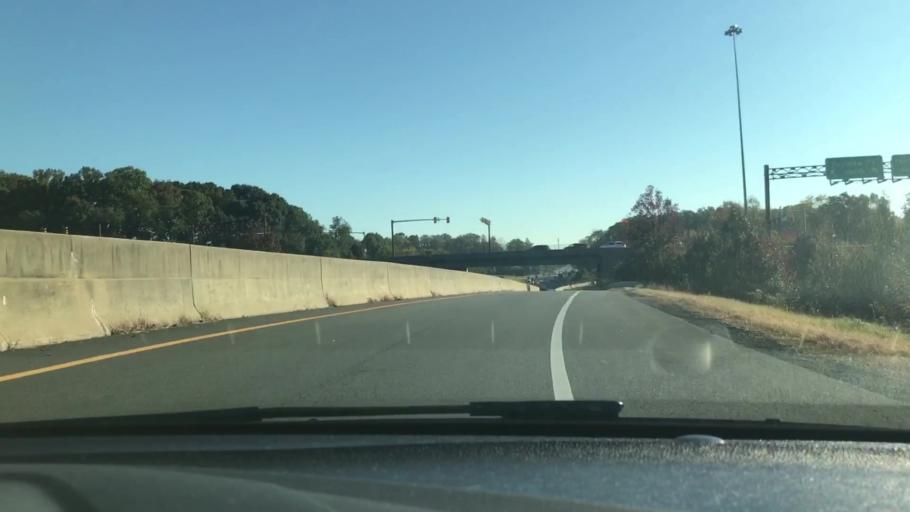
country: US
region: Virginia
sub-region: Fairfax County
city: Merrifield
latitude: 38.8657
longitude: -77.2157
